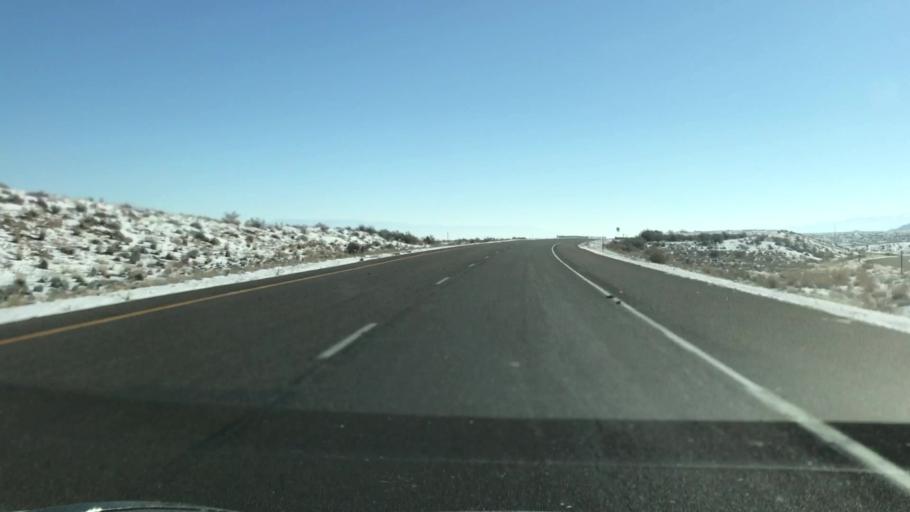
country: US
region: Colorado
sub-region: Mesa County
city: Loma
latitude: 39.2154
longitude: -108.8715
